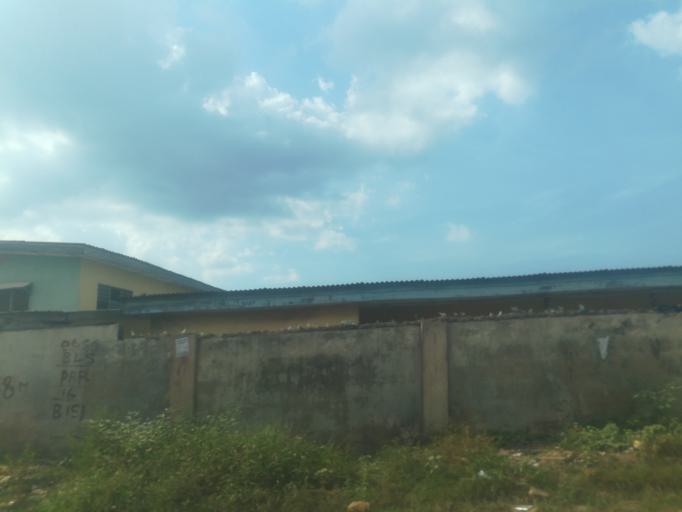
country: NG
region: Ogun
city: Abeokuta
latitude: 7.1147
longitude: 3.3150
